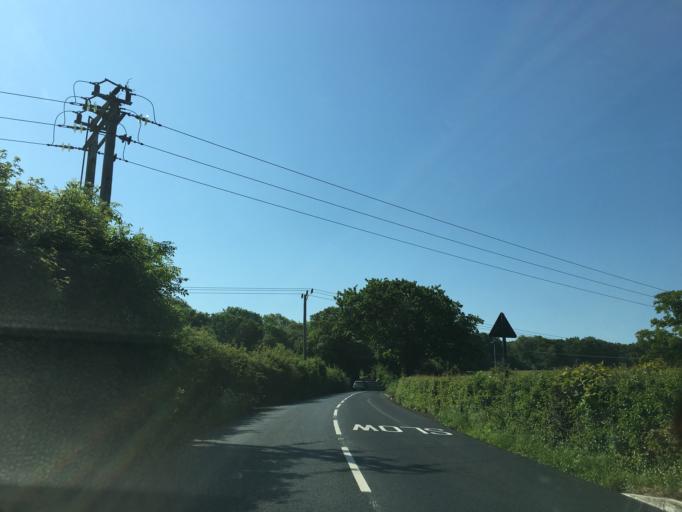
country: GB
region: England
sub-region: Isle of Wight
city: Ryde
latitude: 50.7138
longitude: -1.1660
